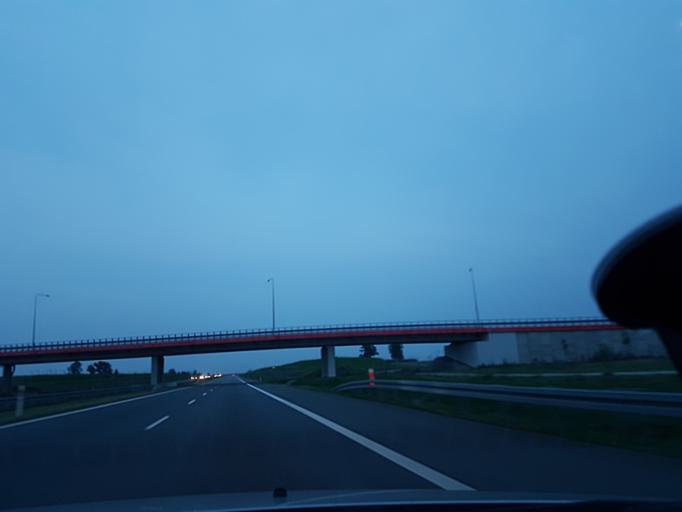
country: PL
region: Lodz Voivodeship
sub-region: Powiat kutnowski
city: Krzyzanow
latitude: 52.1699
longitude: 19.4847
